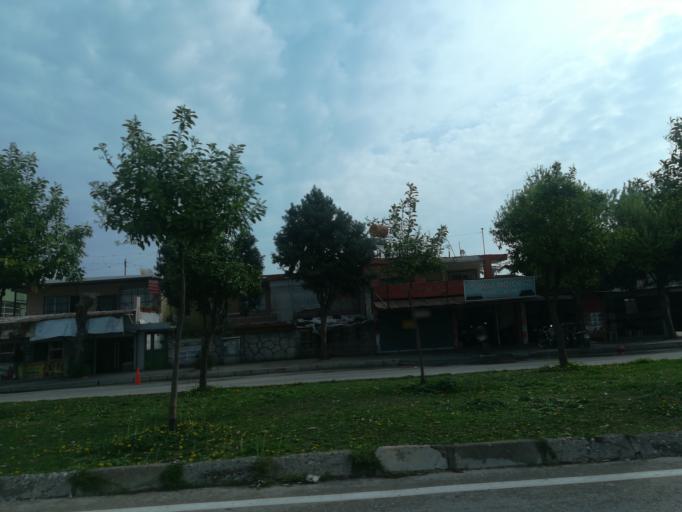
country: TR
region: Adana
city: Yuregir
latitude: 36.9978
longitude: 35.3576
